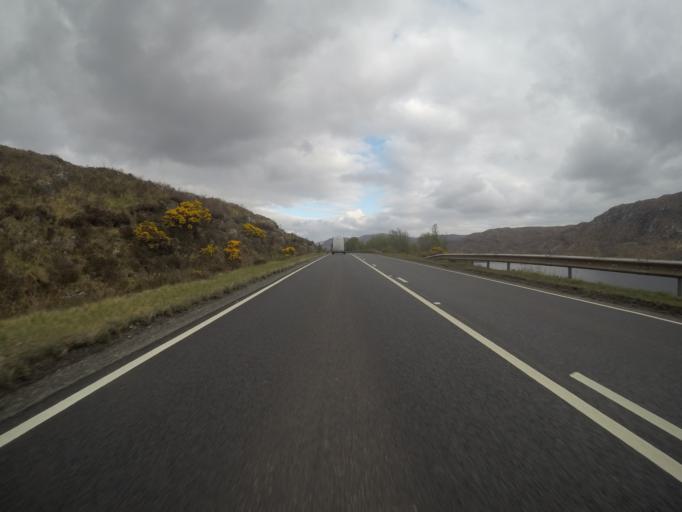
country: GB
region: Scotland
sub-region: Highland
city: Spean Bridge
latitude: 57.1482
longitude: -5.0173
